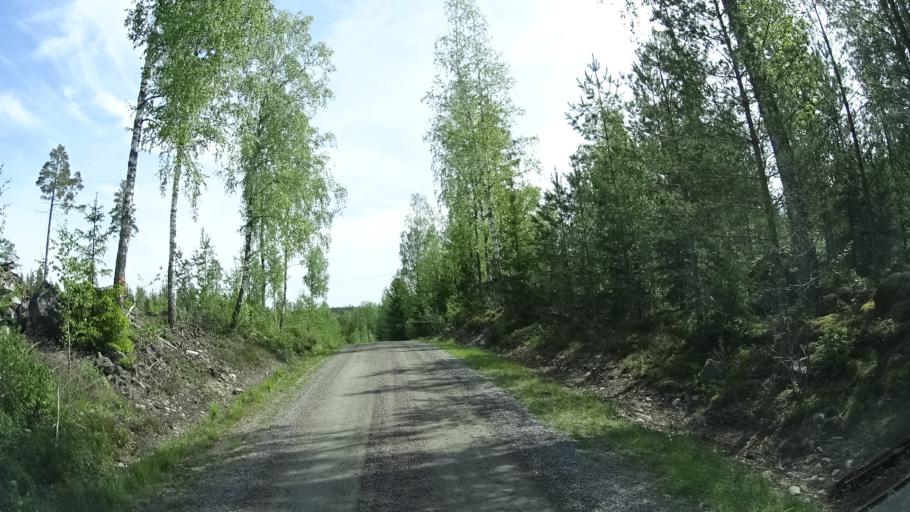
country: SE
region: OEstergoetland
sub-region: Finspangs Kommun
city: Finspang
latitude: 58.7789
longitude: 15.8648
